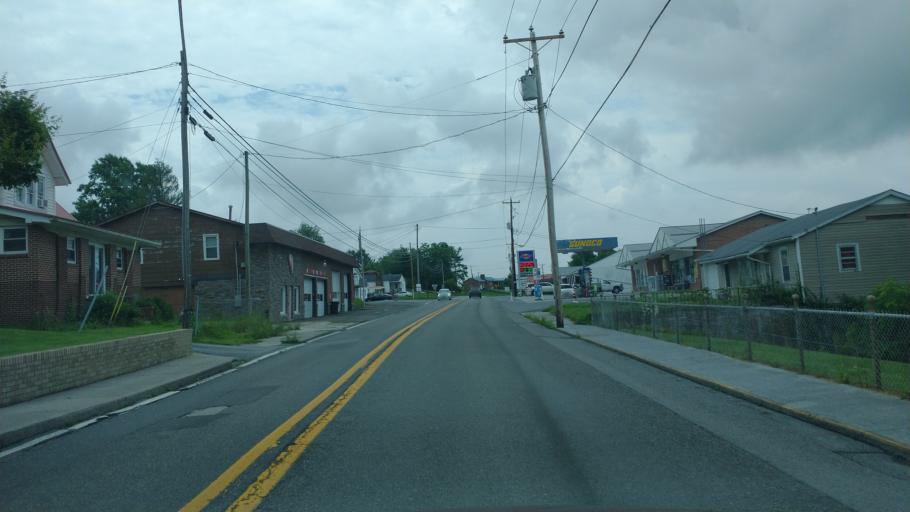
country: US
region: West Virginia
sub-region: Mercer County
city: Athens
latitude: 37.4173
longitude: -81.0157
